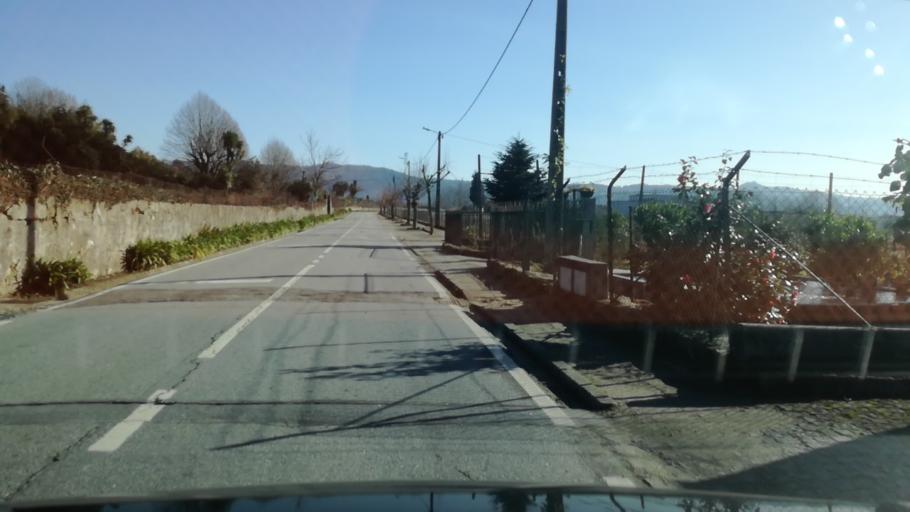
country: PT
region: Braga
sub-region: Guimaraes
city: Ponte
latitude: 41.5208
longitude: -8.3224
